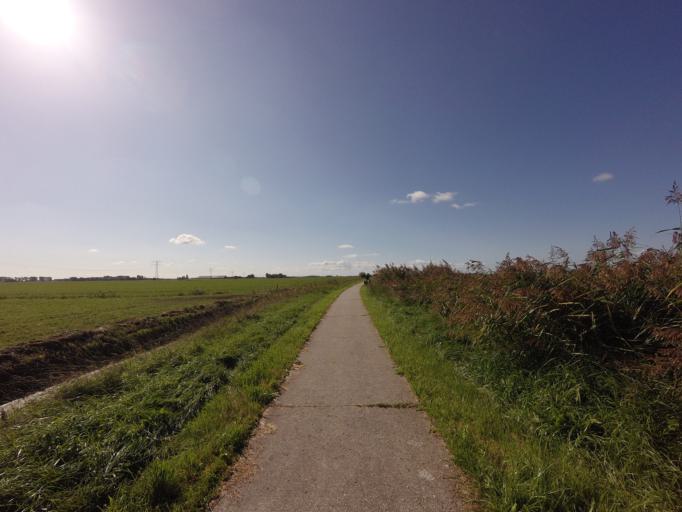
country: NL
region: Friesland
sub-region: Gemeente Boarnsterhim
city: Reduzum
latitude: 53.1428
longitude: 5.7643
